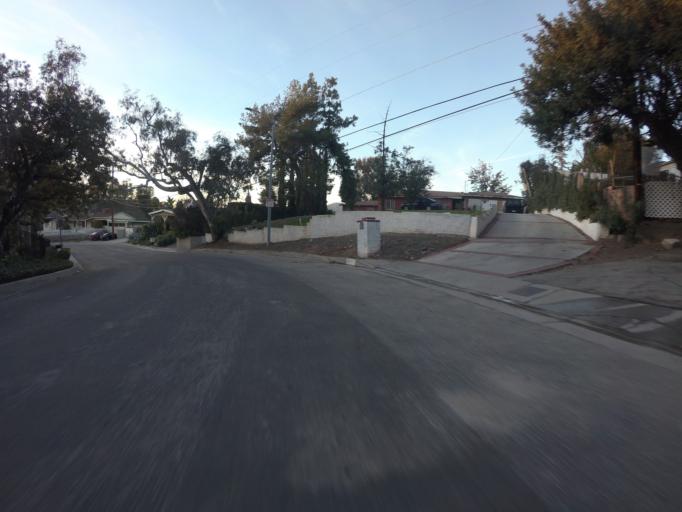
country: US
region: California
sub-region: Los Angeles County
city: San Fernando
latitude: 34.2646
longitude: -118.3531
